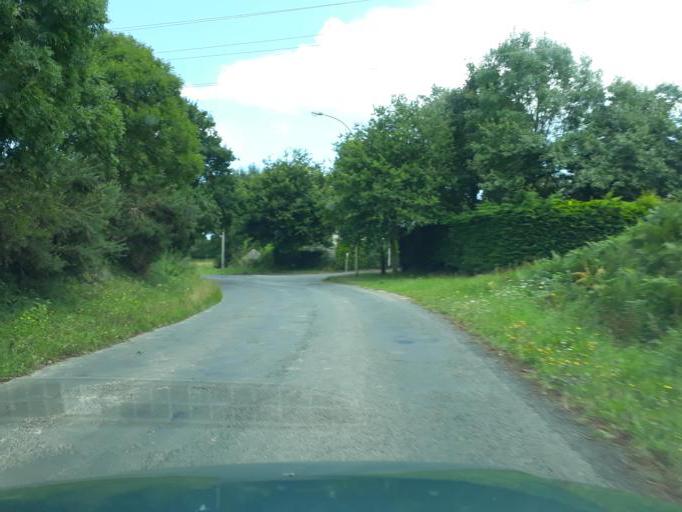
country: FR
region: Brittany
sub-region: Departement des Cotes-d'Armor
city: Paimpol
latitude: 48.7725
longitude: -3.0681
